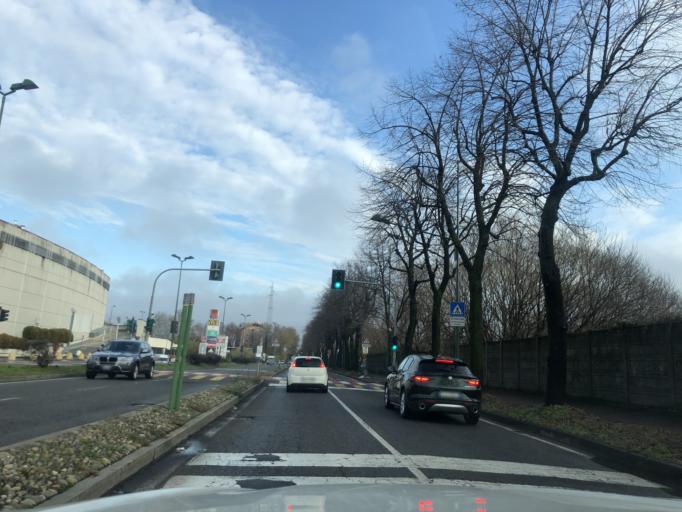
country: IT
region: Lombardy
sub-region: Citta metropolitana di Milano
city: Sesto San Giovanni
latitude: 45.5494
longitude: 9.2577
